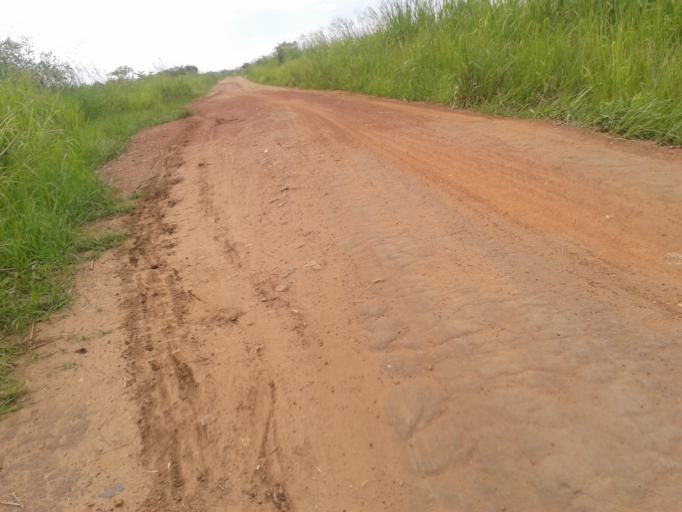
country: UG
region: Northern Region
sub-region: Gulu District
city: Gulu
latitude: 2.8244
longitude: 32.2615
